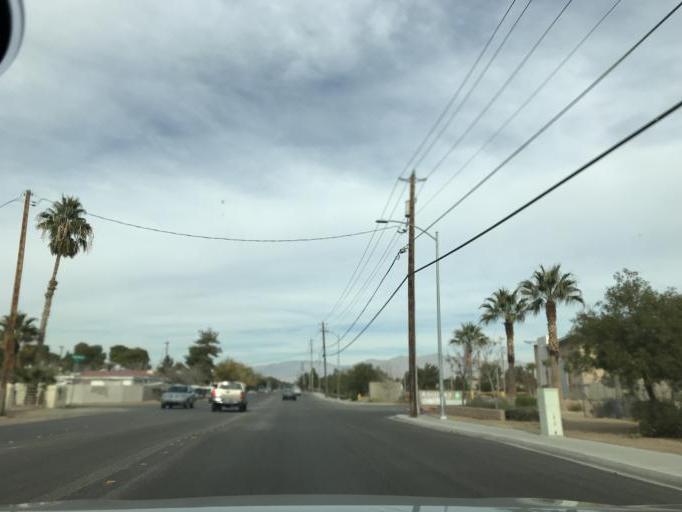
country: US
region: Nevada
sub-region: Clark County
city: Las Vegas
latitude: 36.2065
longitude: -115.2152
